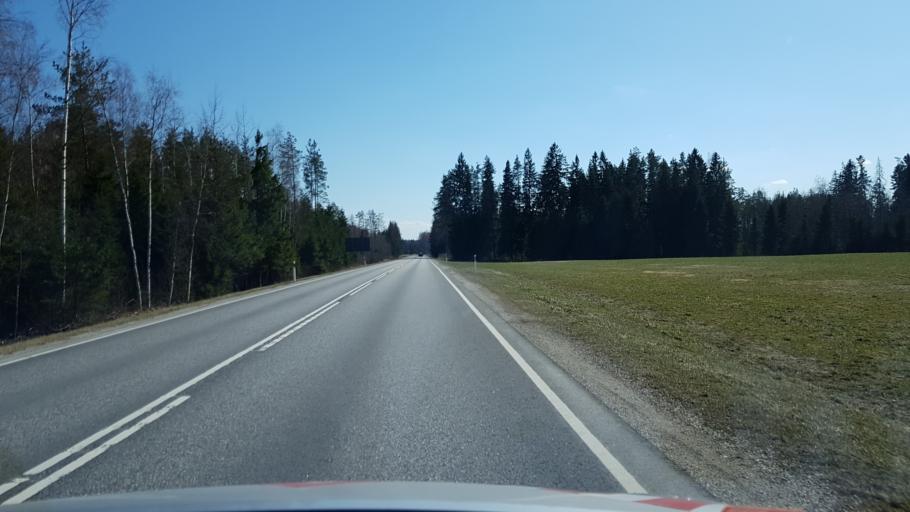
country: EE
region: Jogevamaa
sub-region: Mustvee linn
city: Mustvee
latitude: 58.7053
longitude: 26.8177
